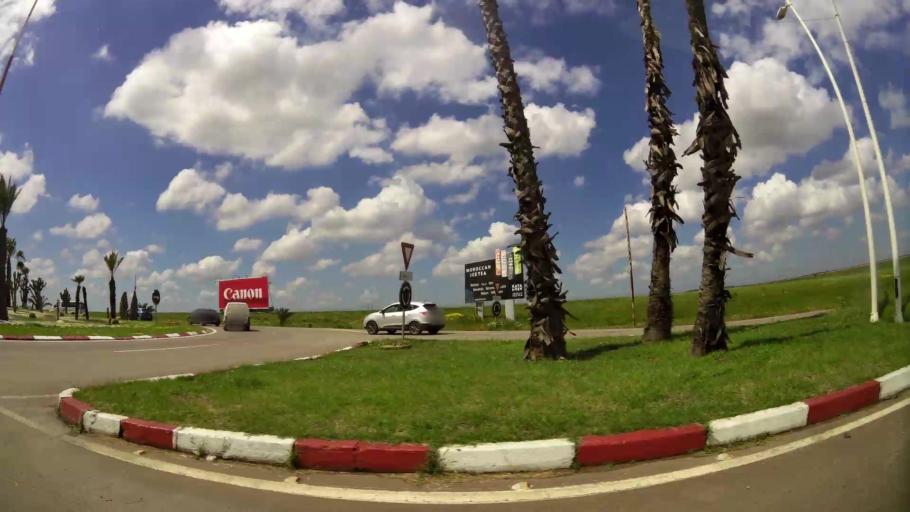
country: MA
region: Chaouia-Ouardigha
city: Nouaseur
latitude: 33.4013
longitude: -7.5699
